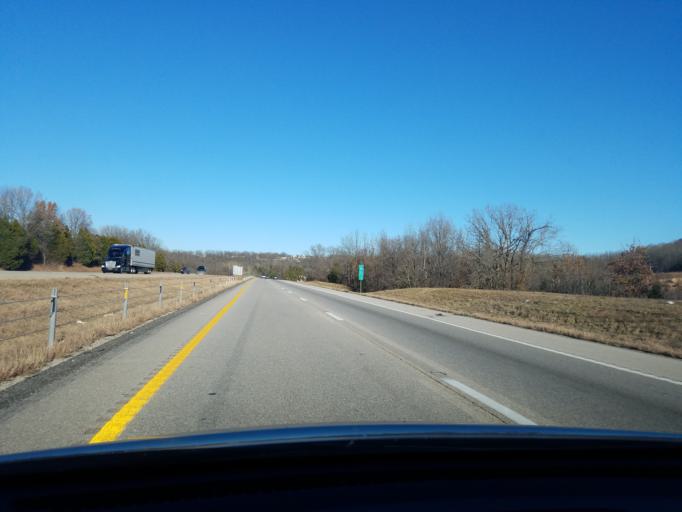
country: US
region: Missouri
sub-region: Pulaski County
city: Waynesville
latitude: 37.8144
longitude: -92.2068
